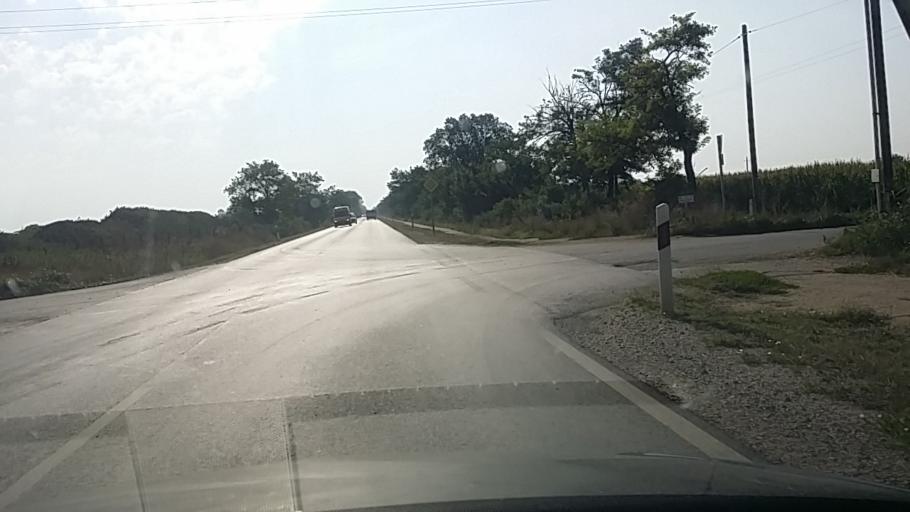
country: HU
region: Bekes
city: Kondoros
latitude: 46.7650
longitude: 20.7760
